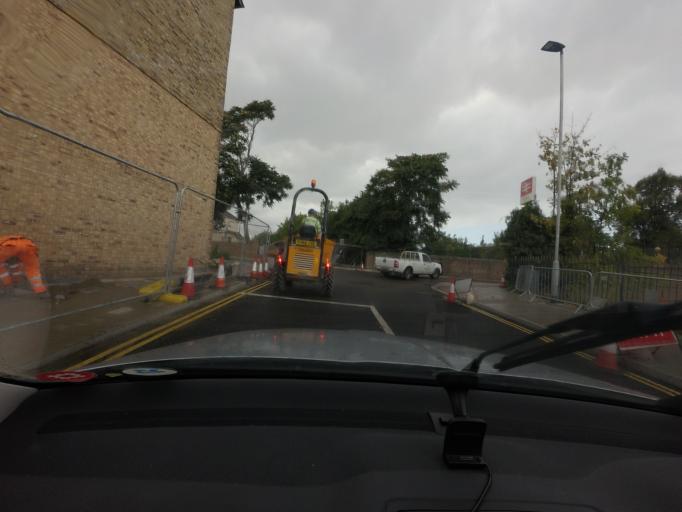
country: GB
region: England
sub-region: Kent
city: Gravesend
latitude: 51.4410
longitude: 0.3651
